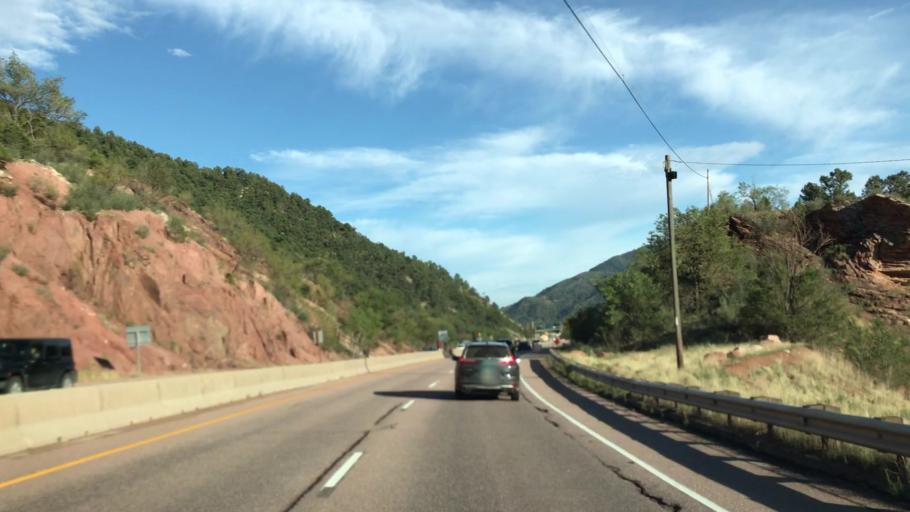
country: US
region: Colorado
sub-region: El Paso County
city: Manitou Springs
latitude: 38.8698
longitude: -104.9243
